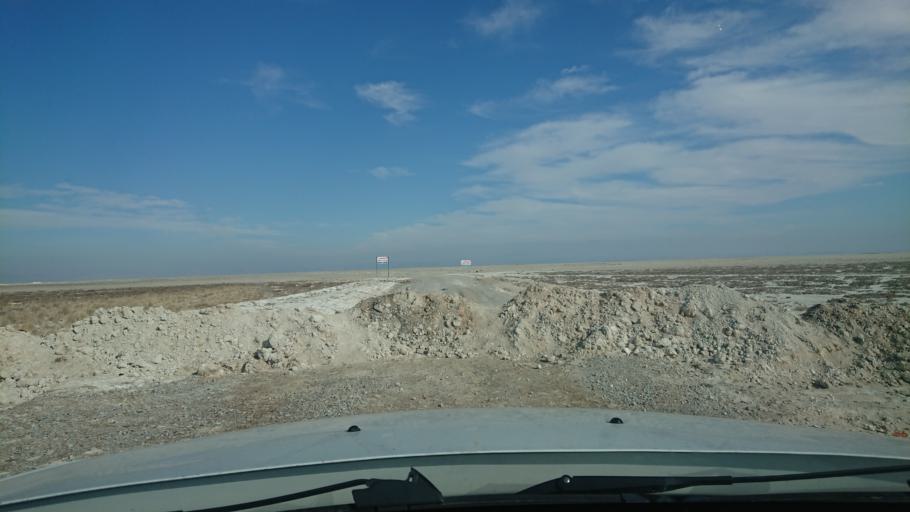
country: TR
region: Aksaray
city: Eskil
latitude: 38.4839
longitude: 33.4762
